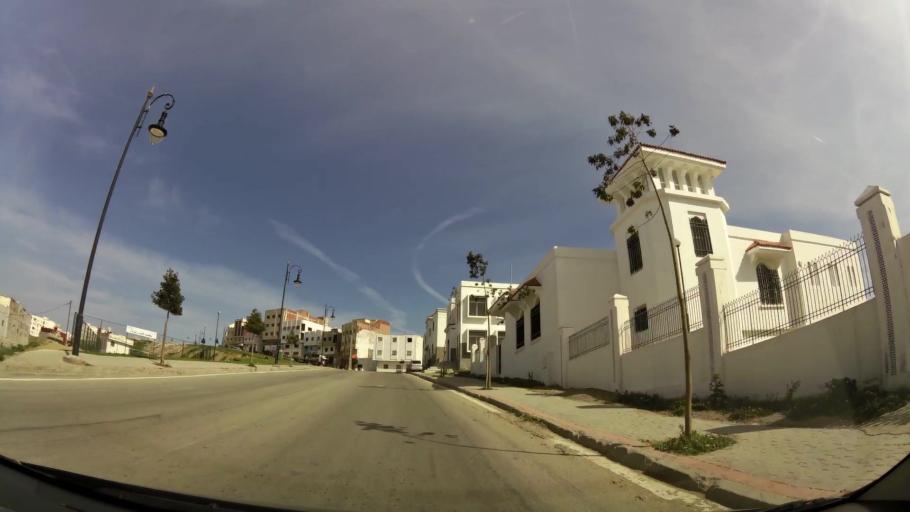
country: MA
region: Tanger-Tetouan
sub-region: Tanger-Assilah
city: Tangier
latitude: 35.7289
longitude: -5.8137
